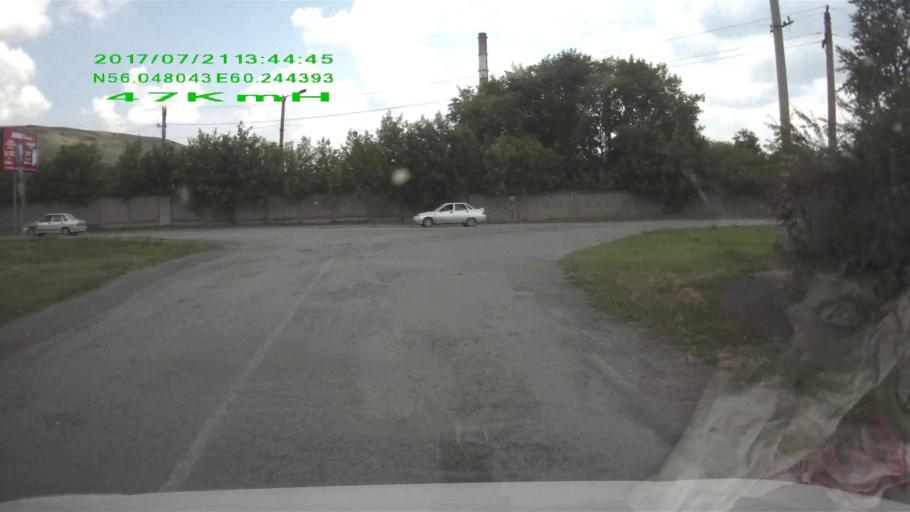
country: RU
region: Chelyabinsk
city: Verkhniy Ufaley
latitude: 56.0478
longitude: 60.2450
